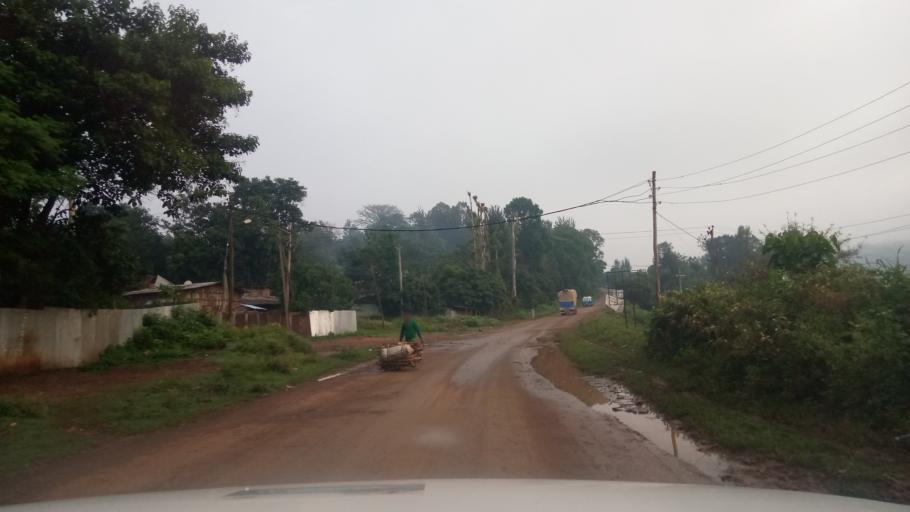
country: ET
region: Oromiya
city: Jima
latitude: 7.6889
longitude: 36.8265
